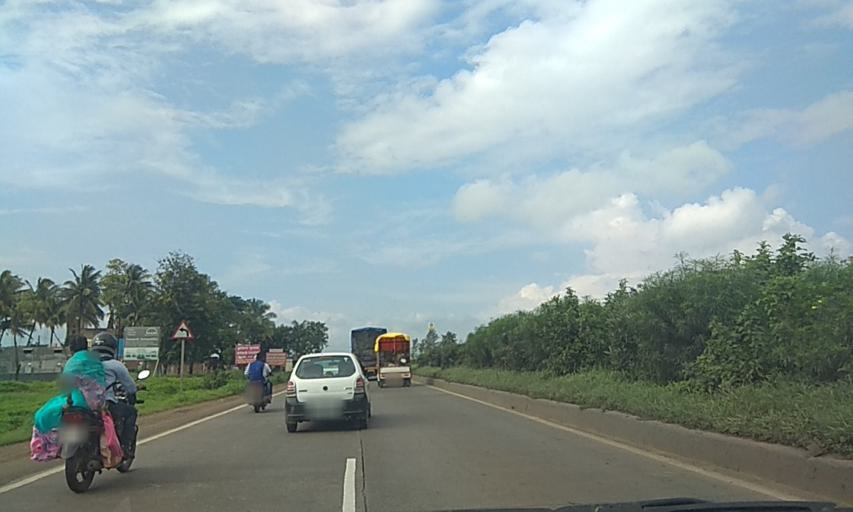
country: IN
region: Maharashtra
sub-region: Kolhapur
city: Kodoli
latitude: 16.8082
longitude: 74.2850
